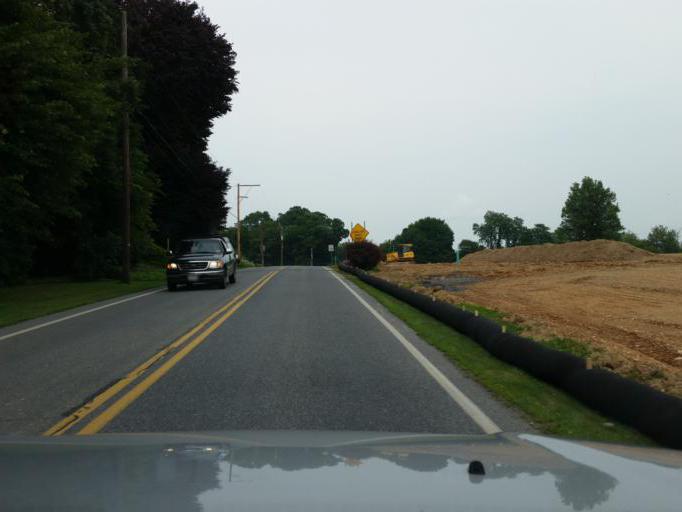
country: US
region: Pennsylvania
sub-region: Lancaster County
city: Manheim
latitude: 40.1510
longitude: -76.3788
